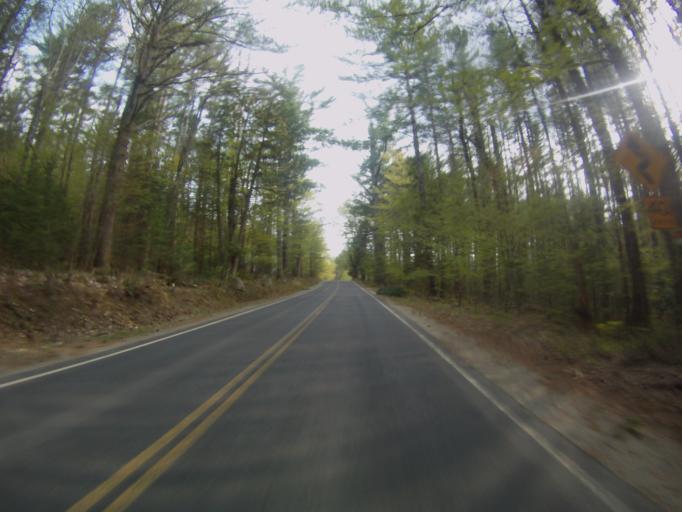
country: US
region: New York
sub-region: Warren County
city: Warrensburg
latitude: 43.8124
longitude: -73.9364
